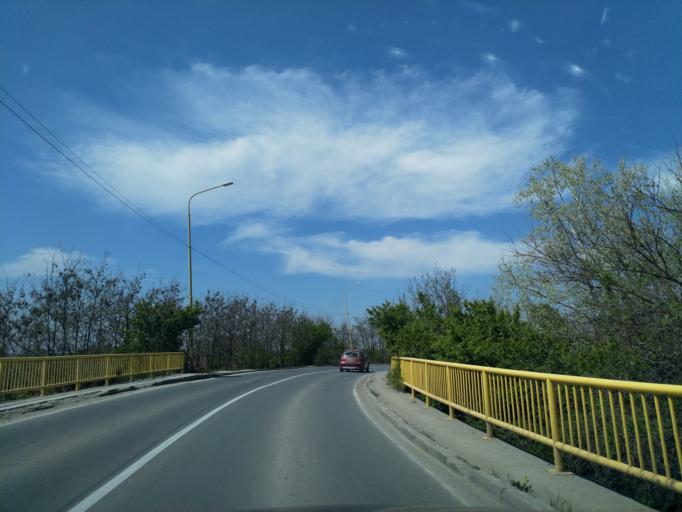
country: RS
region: Central Serbia
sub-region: Belgrade
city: Lazarevac
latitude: 44.3854
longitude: 20.2488
